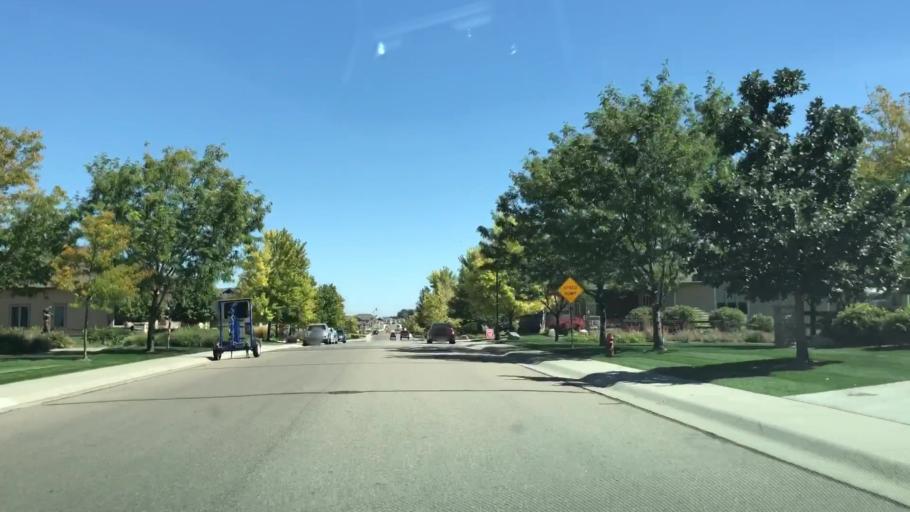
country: US
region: Colorado
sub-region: Weld County
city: Johnstown
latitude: 40.3993
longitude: -104.9781
